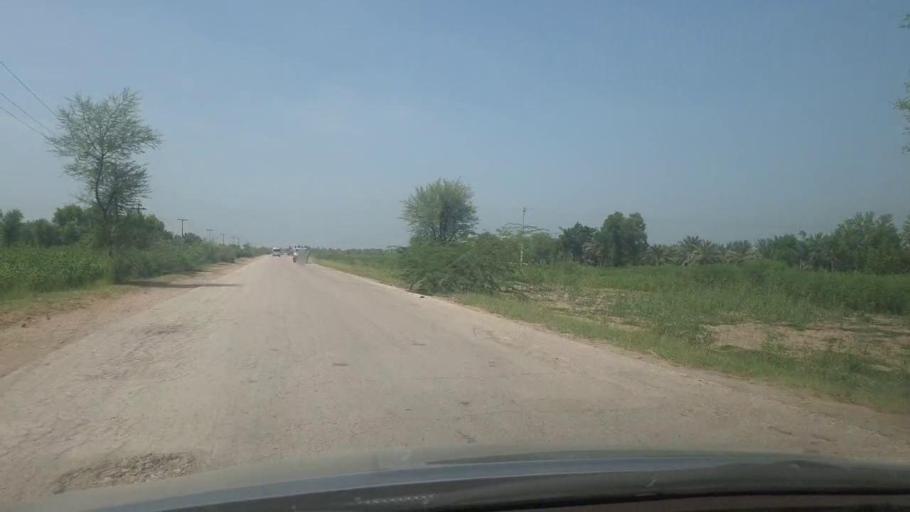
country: PK
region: Sindh
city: Ranipur
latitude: 27.2681
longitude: 68.5937
